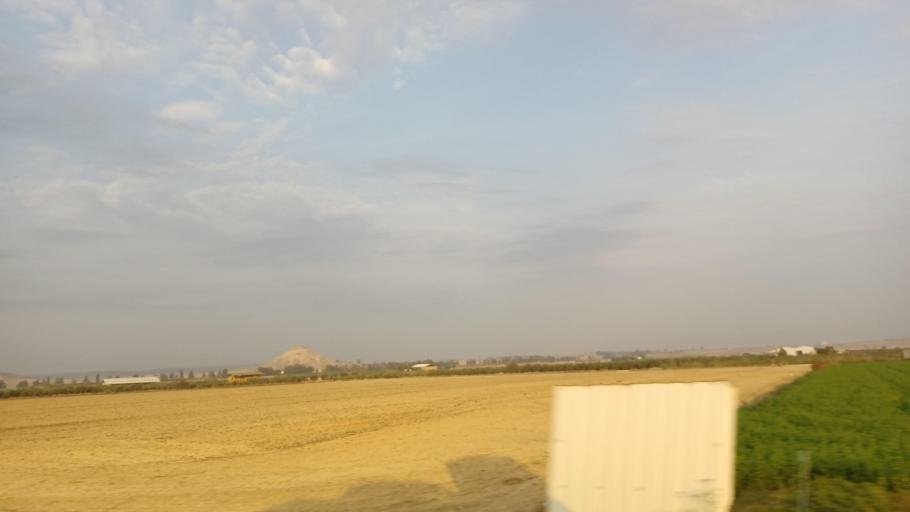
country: CY
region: Larnaka
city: Athienou
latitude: 35.0539
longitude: 33.5099
